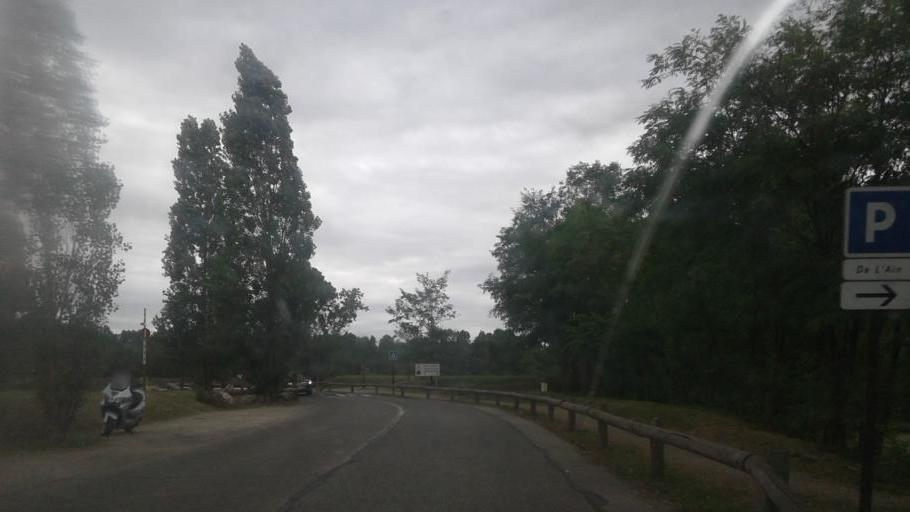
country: FR
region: Rhone-Alpes
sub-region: Departement du Rhone
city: Vaulx-en-Velin
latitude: 45.8056
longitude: 4.9334
